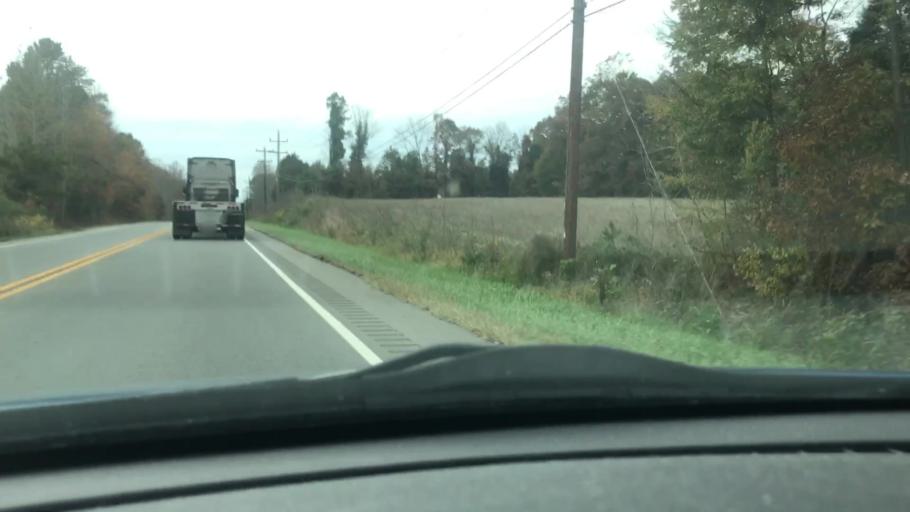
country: US
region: North Carolina
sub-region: Davidson County
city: Lexington
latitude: 35.8046
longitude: -80.1661
